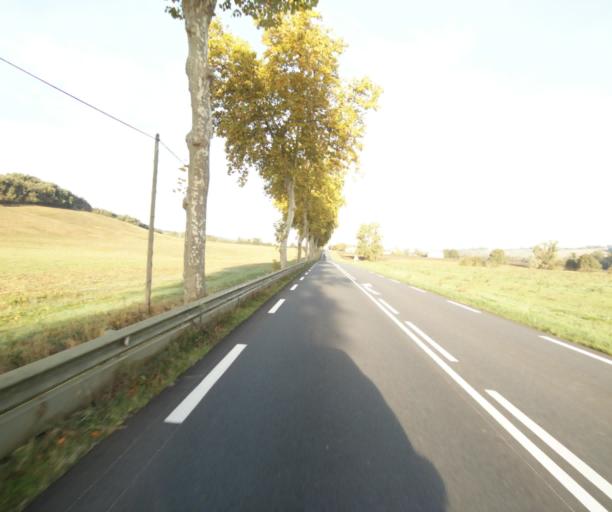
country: FR
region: Midi-Pyrenees
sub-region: Departement du Tarn-et-Garonne
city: Nohic
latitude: 43.9362
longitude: 1.4827
